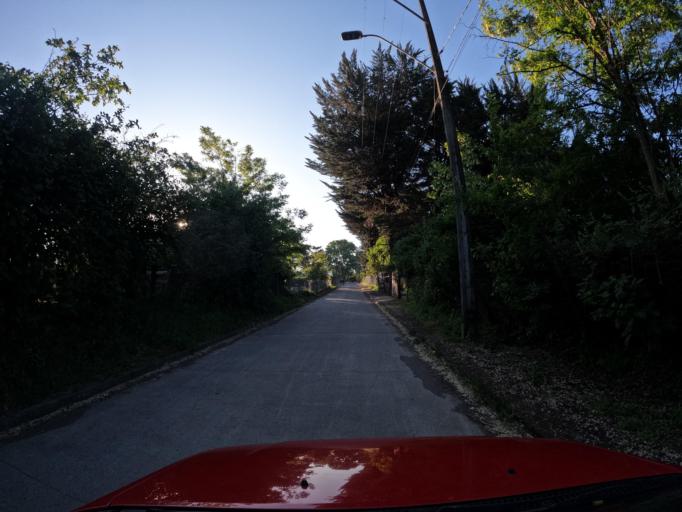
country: CL
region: Biobio
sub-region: Provincia de Concepcion
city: Lota
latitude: -37.1680
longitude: -72.9441
